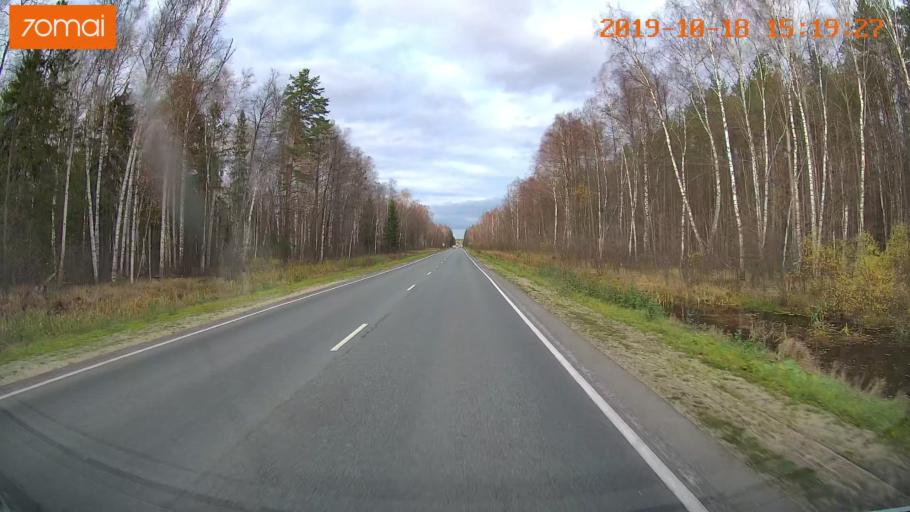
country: RU
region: Vladimir
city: Anopino
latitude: 55.6733
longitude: 40.7378
